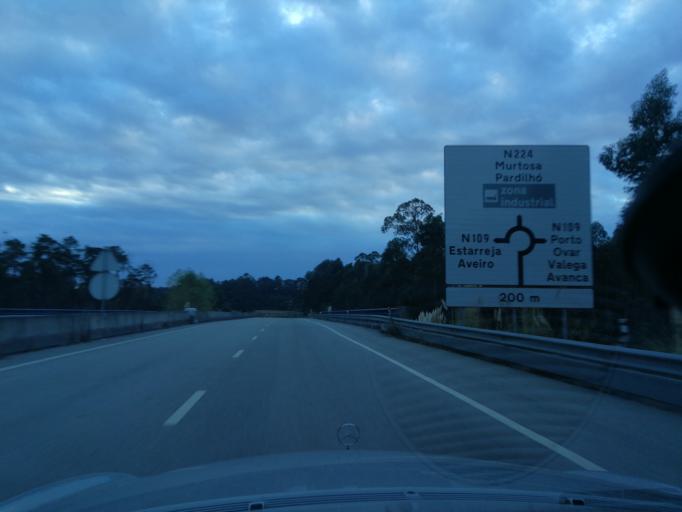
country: PT
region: Aveiro
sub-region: Estarreja
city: Beduido
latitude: 40.7832
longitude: -8.5616
